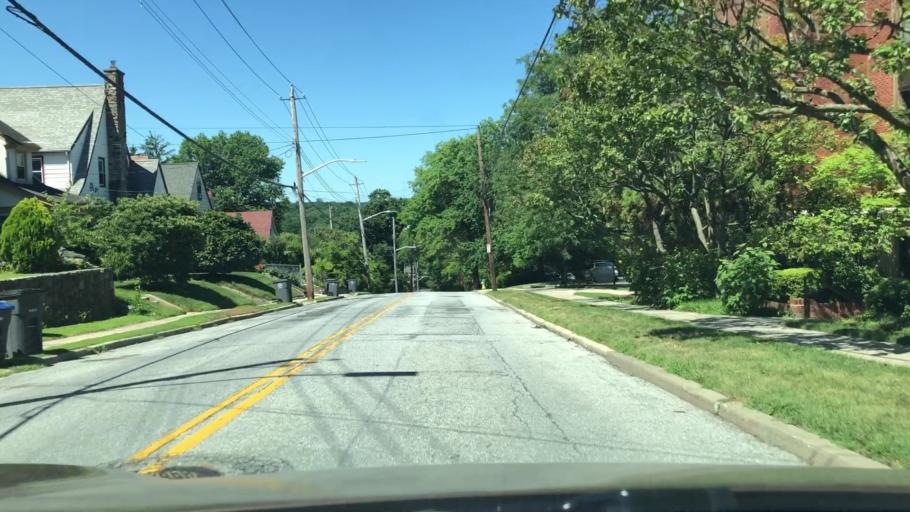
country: US
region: New York
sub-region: Westchester County
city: White Plains
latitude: 41.0301
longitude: -73.7821
